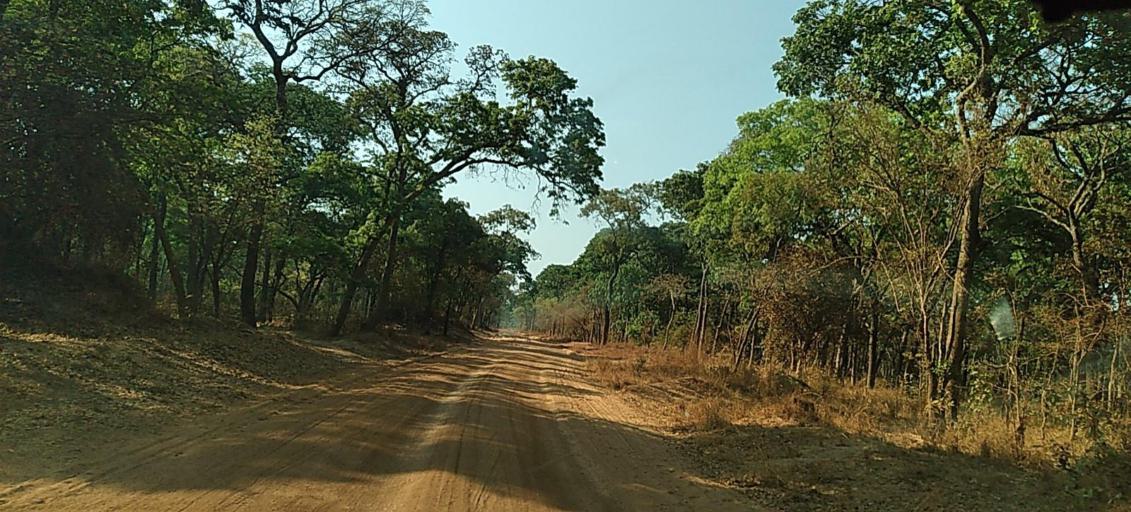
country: ZM
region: North-Western
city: Kasempa
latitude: -13.6528
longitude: 26.0059
